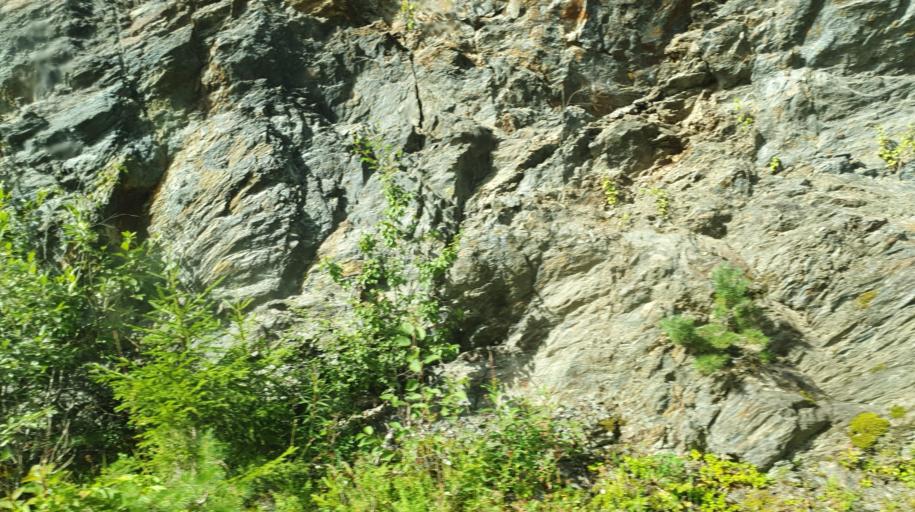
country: NO
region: Nord-Trondelag
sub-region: Levanger
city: Skogn
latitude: 63.5899
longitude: 11.2515
